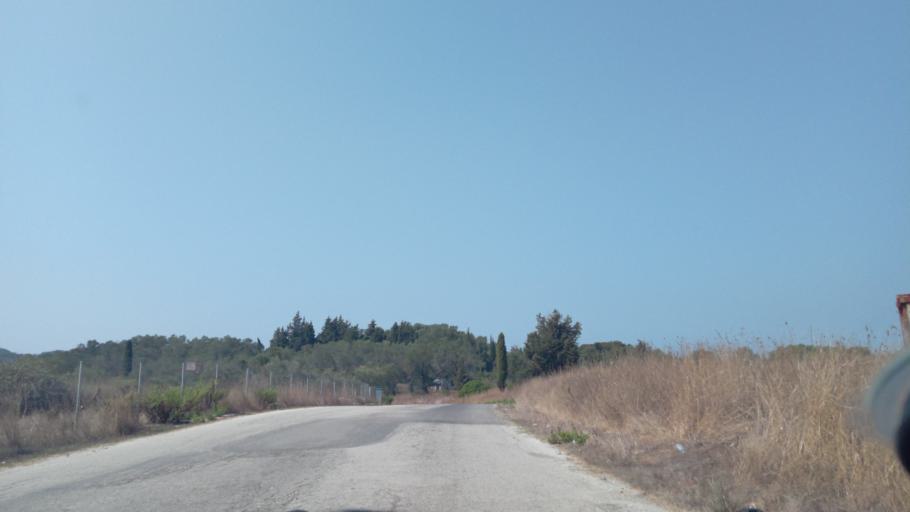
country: GR
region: Ionian Islands
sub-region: Nomos Kerkyras
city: Perivoli
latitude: 39.4175
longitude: 20.0315
